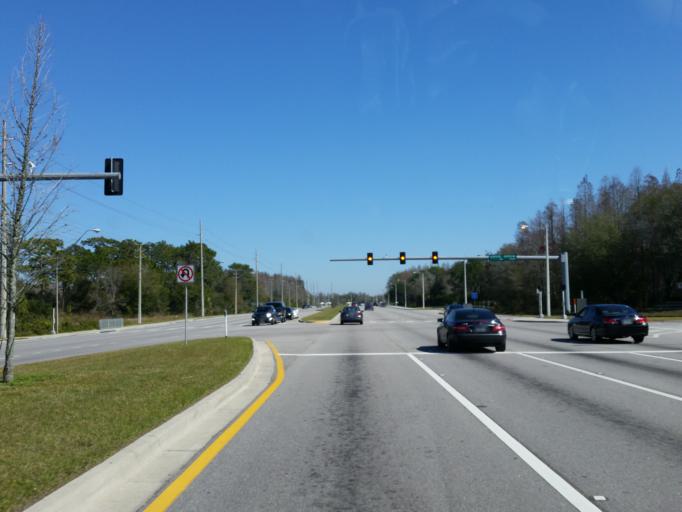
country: US
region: Florida
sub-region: Hillsborough County
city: Pebble Creek
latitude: 28.1376
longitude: -82.3585
